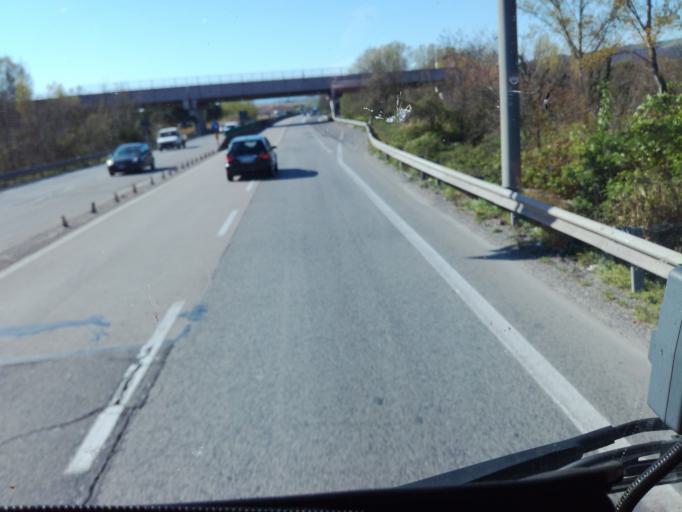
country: IT
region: Umbria
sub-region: Provincia di Perugia
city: Via Lippia
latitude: 43.1030
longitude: 12.4765
